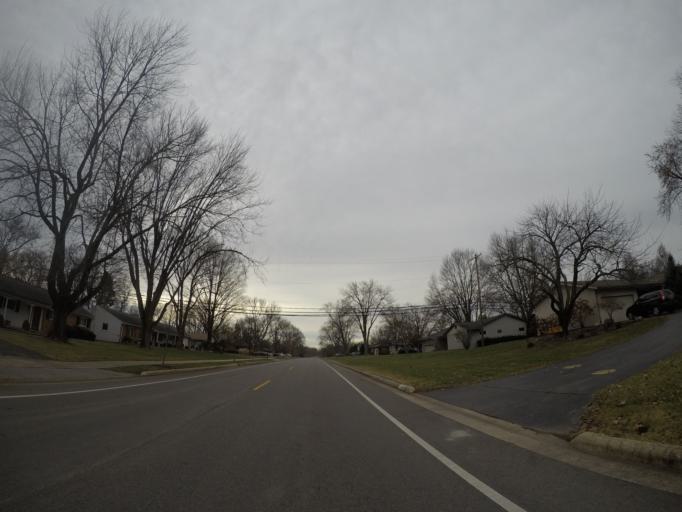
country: US
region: Ohio
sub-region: Franklin County
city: Upper Arlington
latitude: 40.0355
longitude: -83.0716
